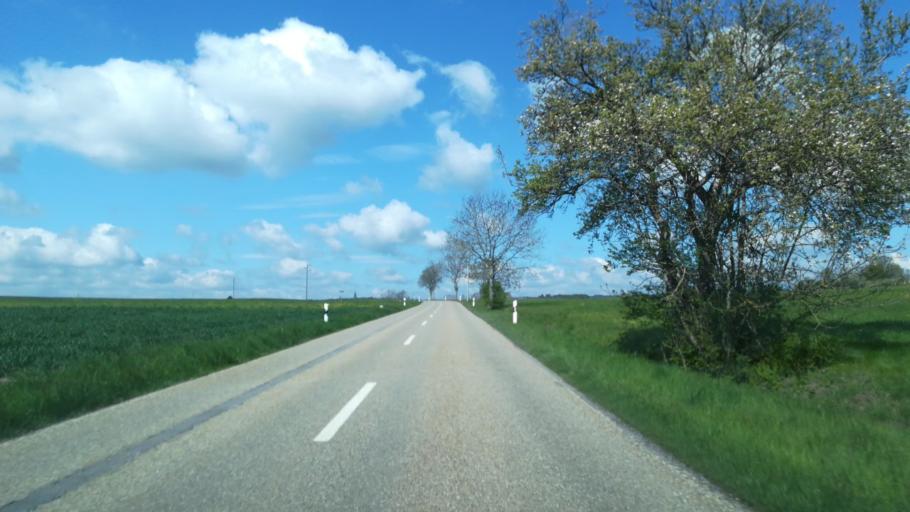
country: DE
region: Baden-Wuerttemberg
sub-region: Freiburg Region
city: Uhlingen-Birkendorf
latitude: 47.7513
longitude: 8.3240
